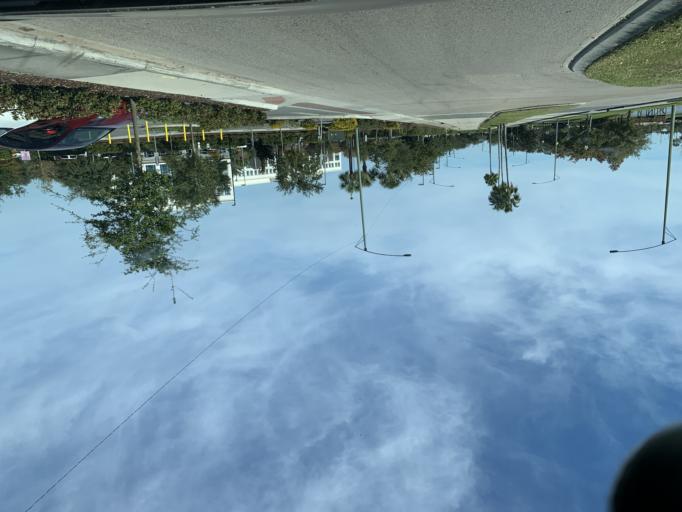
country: US
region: Florida
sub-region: Orange County
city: Oak Ridge
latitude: 28.4845
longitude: -81.4354
